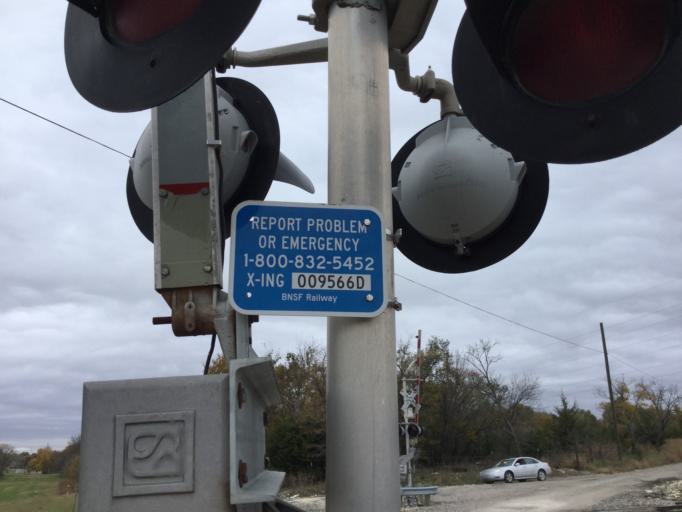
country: US
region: Kansas
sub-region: Butler County
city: El Dorado
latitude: 37.7999
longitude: -96.8620
